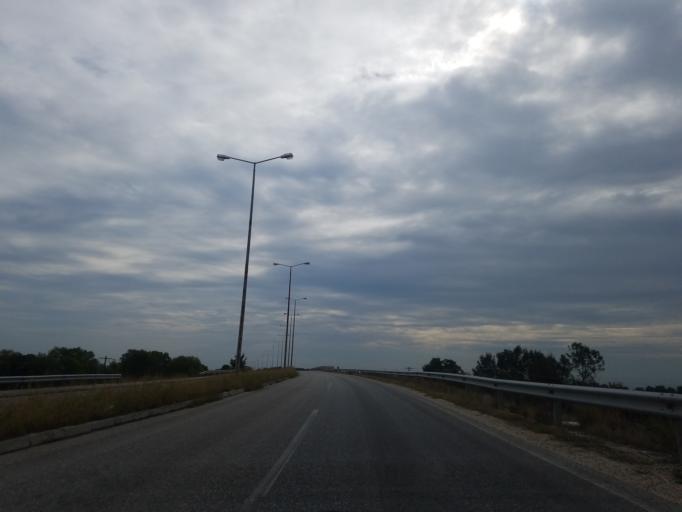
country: GR
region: Thessaly
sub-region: Trikala
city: Pyrgetos
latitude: 39.5208
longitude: 21.7552
